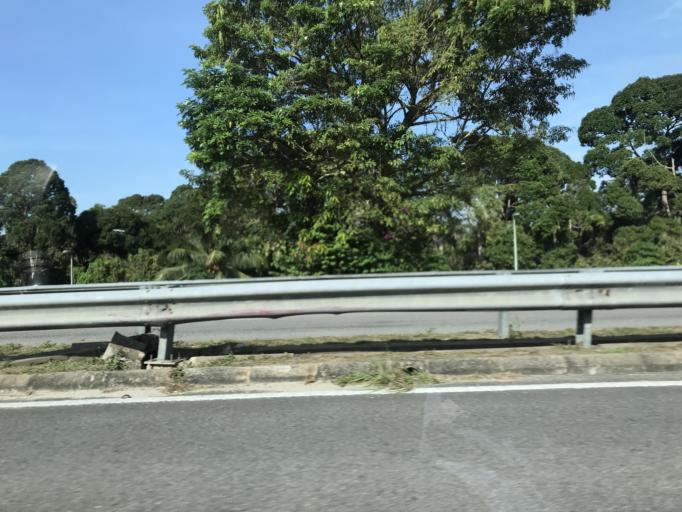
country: MY
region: Kelantan
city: Pasir Mas
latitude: 6.0600
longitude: 102.2100
